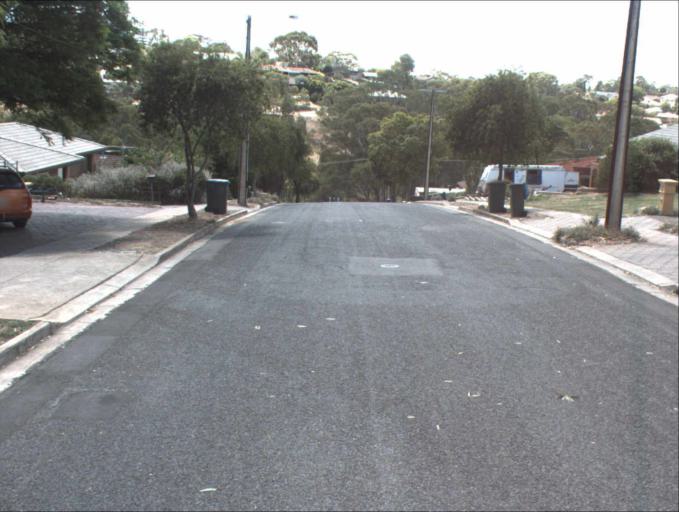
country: AU
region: South Australia
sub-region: Port Adelaide Enfield
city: Gilles Plains
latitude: -34.8419
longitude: 138.6512
